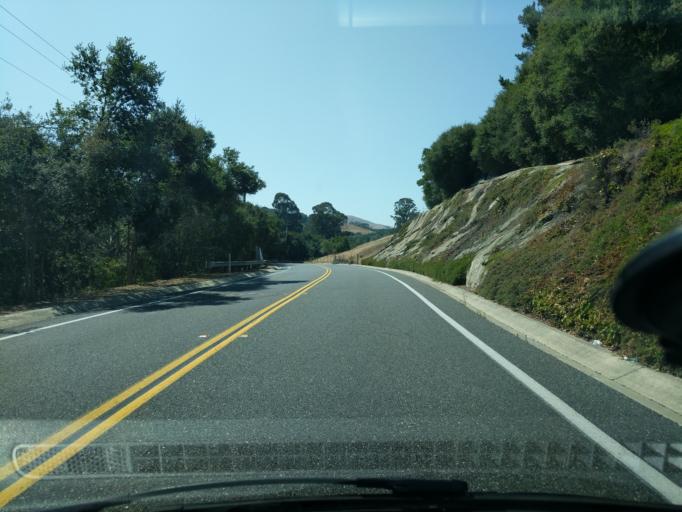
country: US
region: California
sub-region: Contra Costa County
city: San Ramon
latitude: 37.7621
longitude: -121.9849
